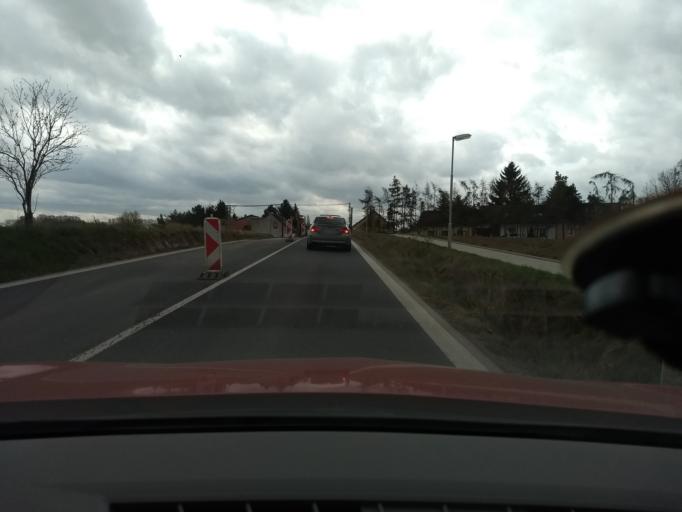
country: CZ
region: Central Bohemia
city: Unhost'
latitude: 50.1128
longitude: 14.1330
